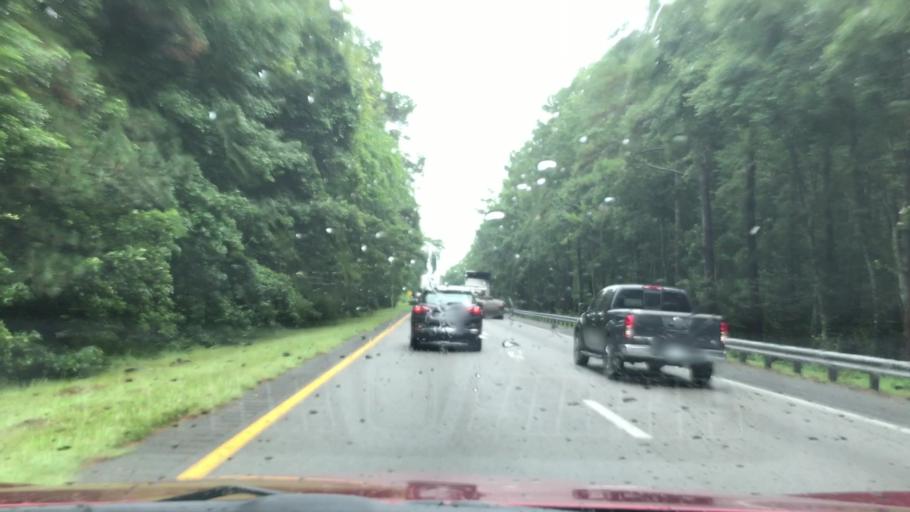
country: US
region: South Carolina
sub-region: Dorchester County
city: Ridgeville
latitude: 33.1014
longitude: -80.2443
